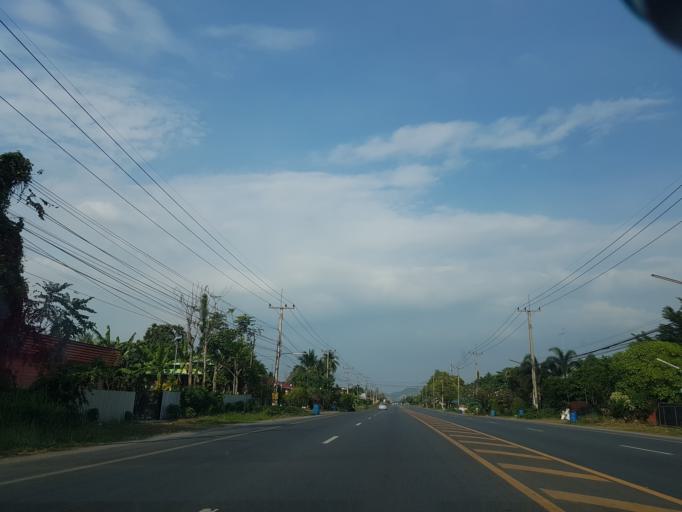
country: TH
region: Sara Buri
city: Ban Mo
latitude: 14.6388
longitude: 100.7552
